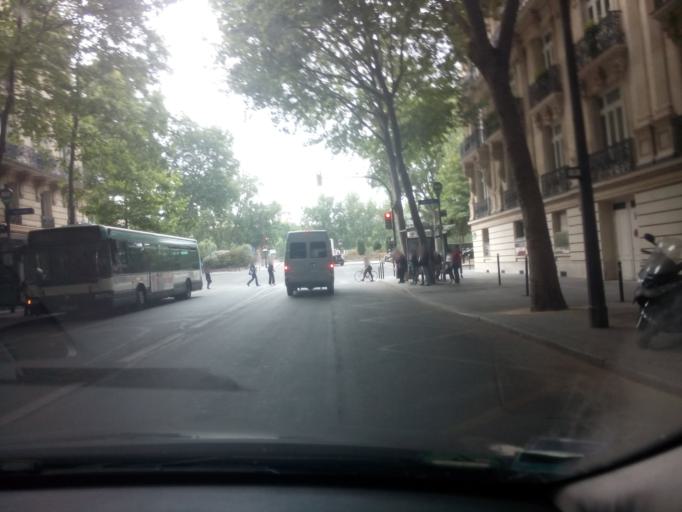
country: FR
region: Ile-de-France
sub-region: Departement des Hauts-de-Seine
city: Levallois-Perret
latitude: 48.8600
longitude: 2.2970
